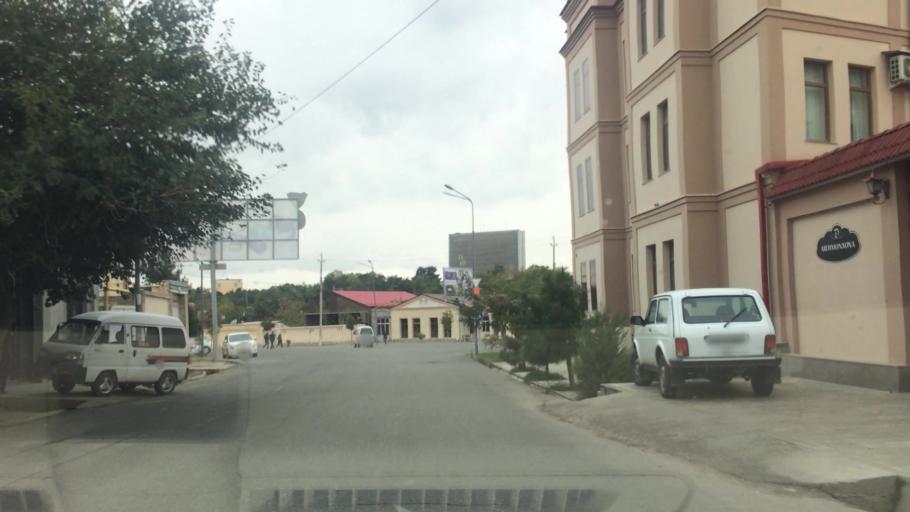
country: UZ
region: Samarqand
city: Samarqand
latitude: 39.6583
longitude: 66.9715
